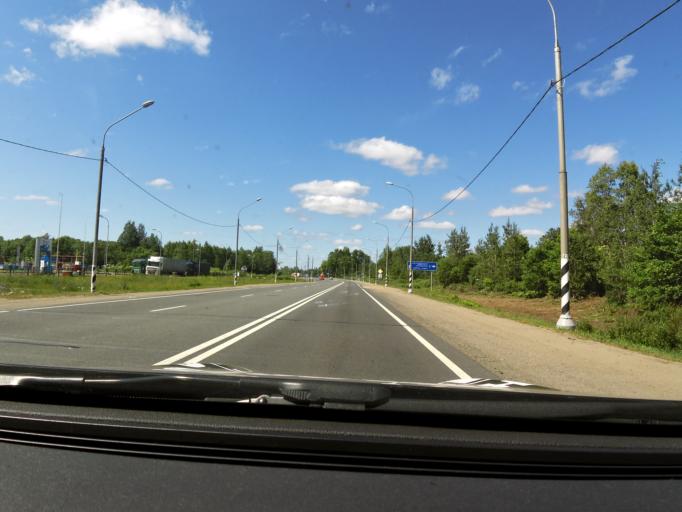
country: RU
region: Novgorod
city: Valday
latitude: 57.9877
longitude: 33.2029
